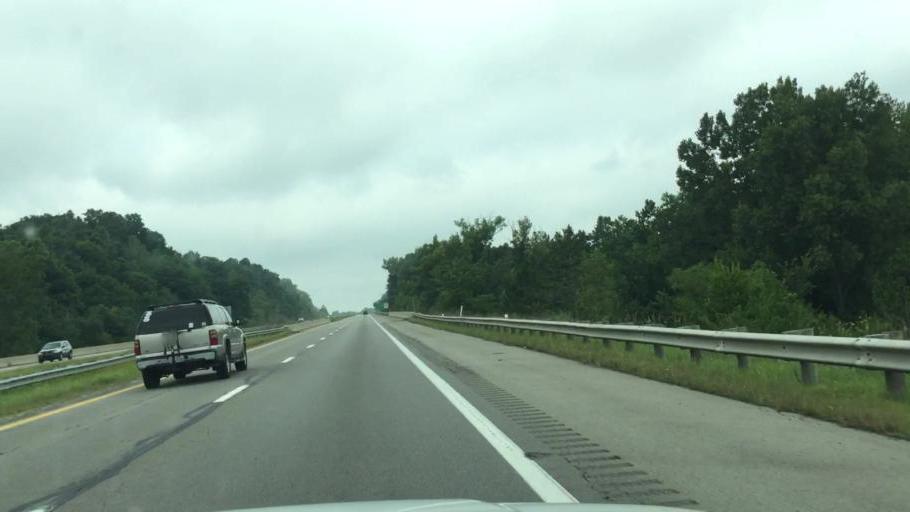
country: US
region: Ohio
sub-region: Logan County
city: Bellefontaine
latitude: 40.3308
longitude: -83.6816
